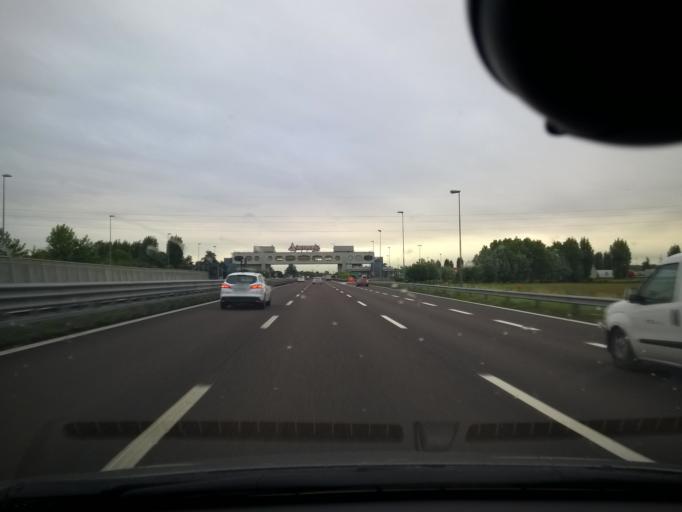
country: IT
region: Veneto
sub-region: Provincia di Padova
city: Limena
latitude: 45.4490
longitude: 11.8426
